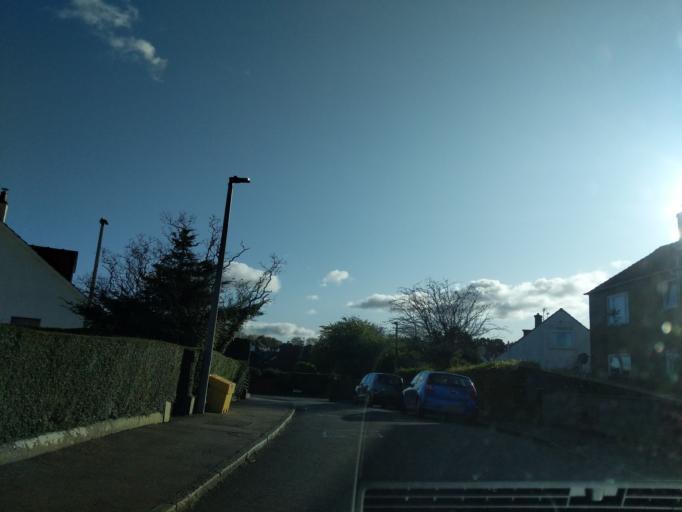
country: GB
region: Scotland
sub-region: Edinburgh
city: Colinton
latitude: 55.9695
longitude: -3.2722
